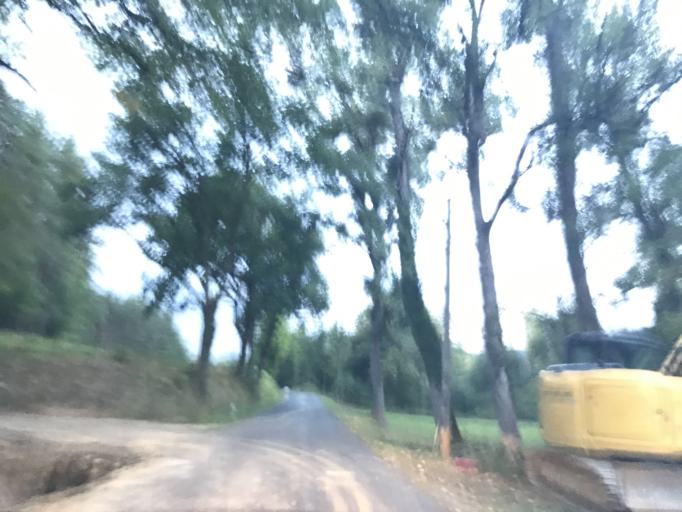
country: FR
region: Auvergne
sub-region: Departement du Puy-de-Dome
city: Escoutoux
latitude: 45.8138
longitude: 3.5626
